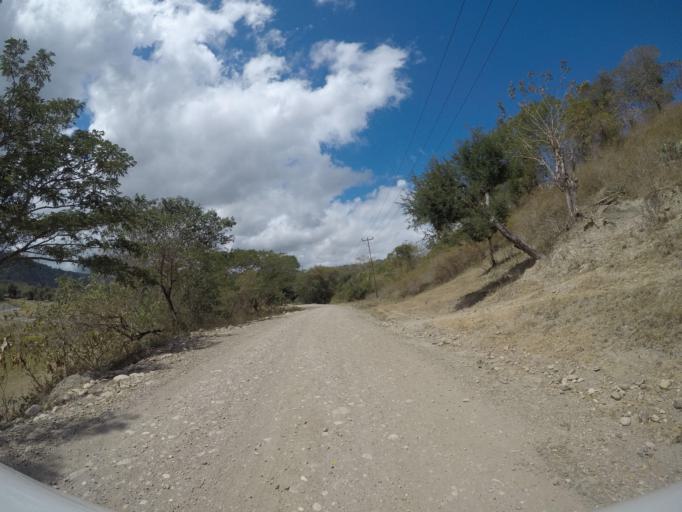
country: TL
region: Lautem
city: Lospalos
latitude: -8.4872
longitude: 126.8191
